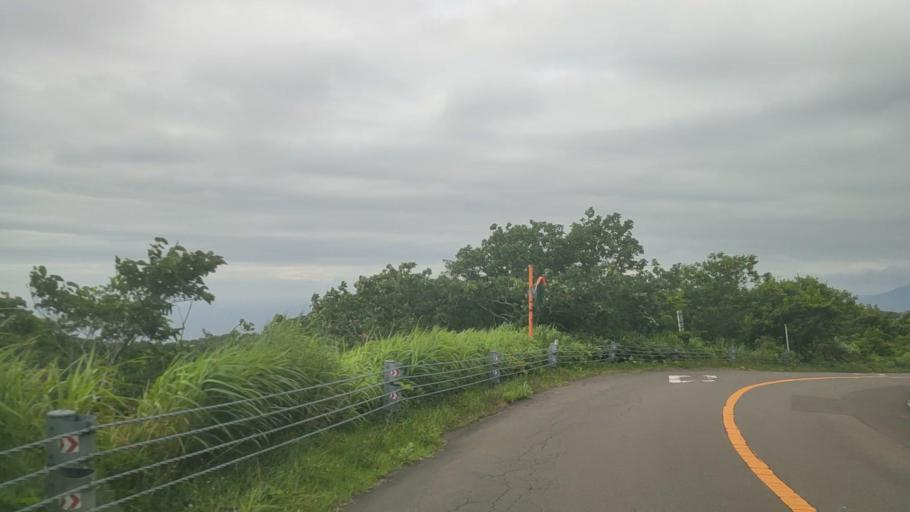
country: JP
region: Hokkaido
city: Hakodate
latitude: 41.7583
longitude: 140.7042
